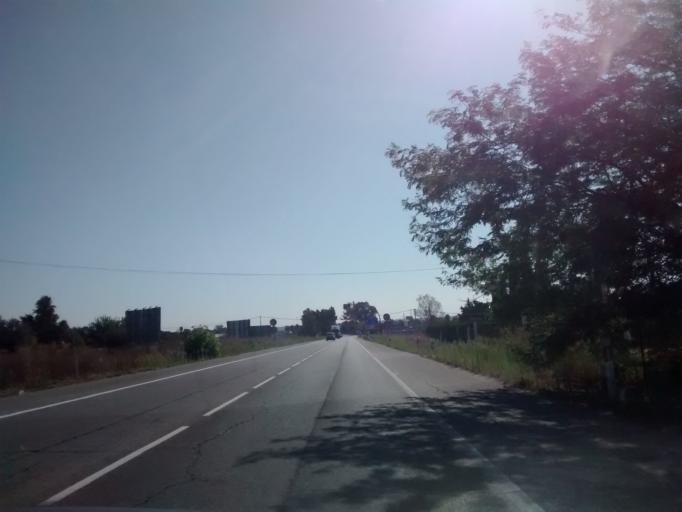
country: ES
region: Andalusia
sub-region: Provincia de Cadiz
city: Jerez de la Frontera
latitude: 36.7014
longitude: -6.0900
